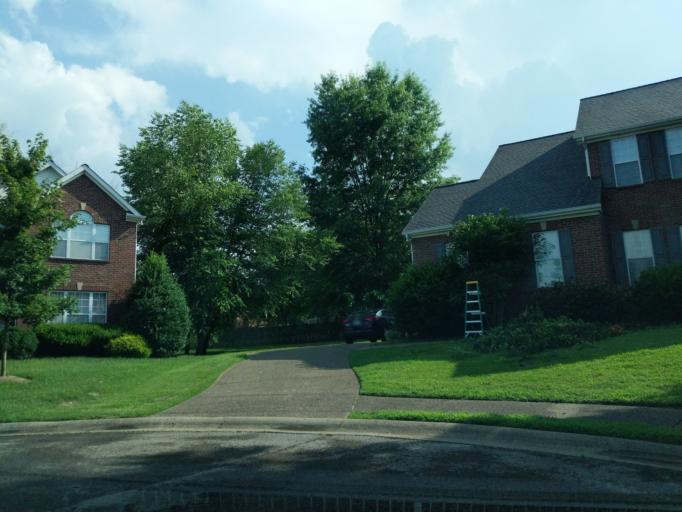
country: US
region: Tennessee
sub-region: Cheatham County
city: Pegram
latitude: 36.0369
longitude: -86.9606
